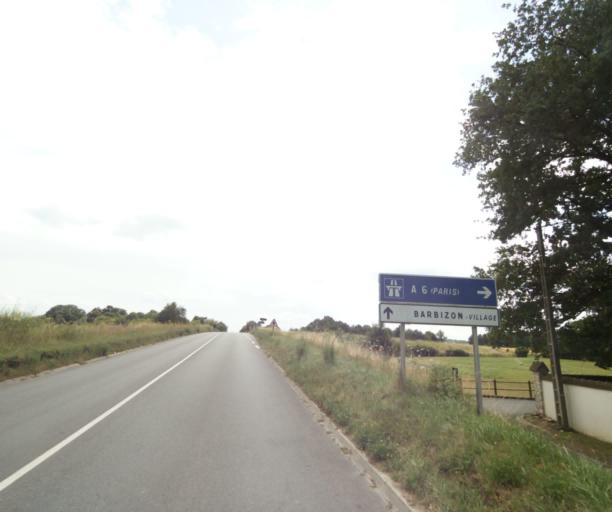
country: FR
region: Ile-de-France
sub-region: Departement de Seine-et-Marne
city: Chailly-en-Biere
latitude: 48.4573
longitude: 2.6060
